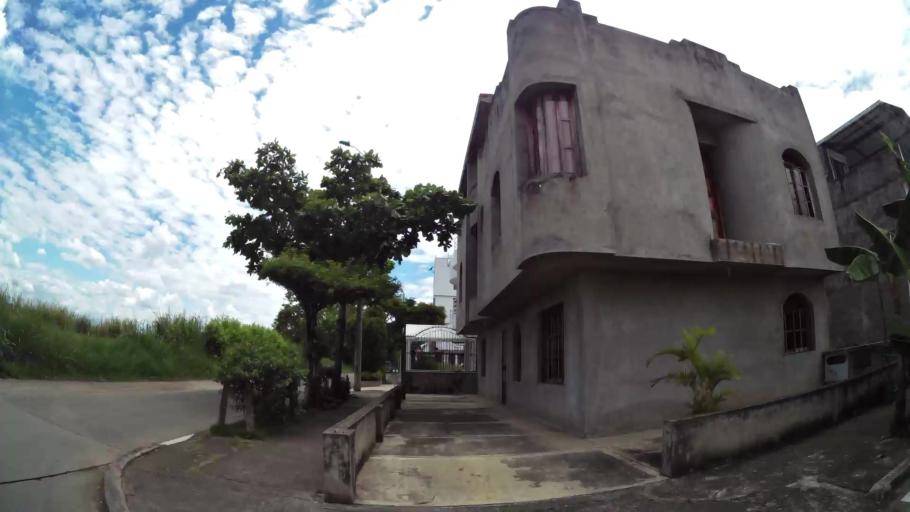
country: CO
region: Valle del Cauca
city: Cali
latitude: 3.3822
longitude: -76.5142
